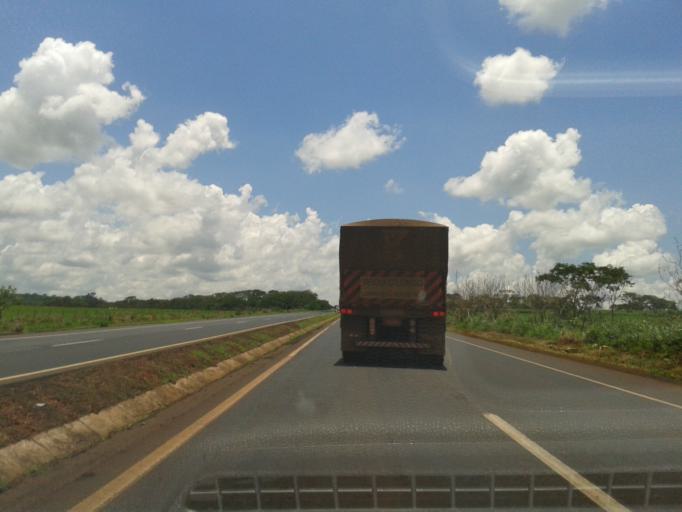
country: BR
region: Minas Gerais
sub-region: Centralina
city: Centralina
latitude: -18.6112
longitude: -49.1911
